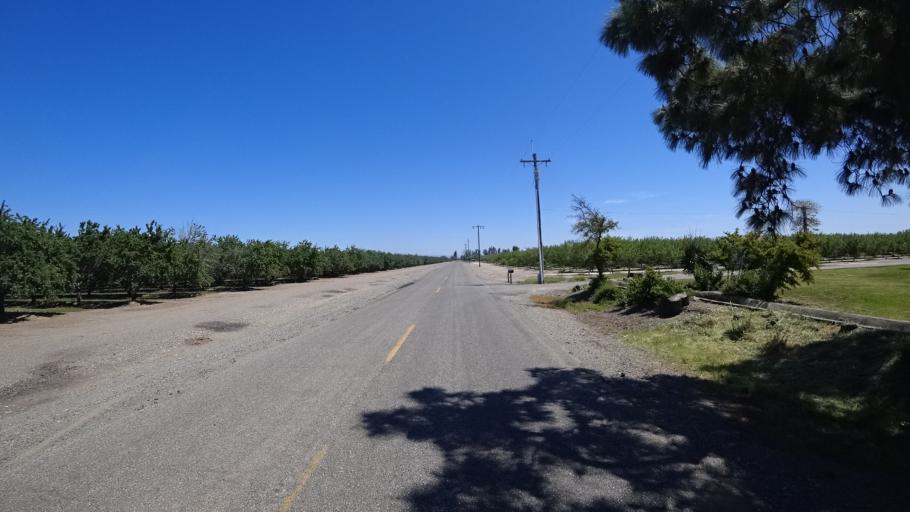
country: US
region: California
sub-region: Glenn County
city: Orland
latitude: 39.7251
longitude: -122.1257
